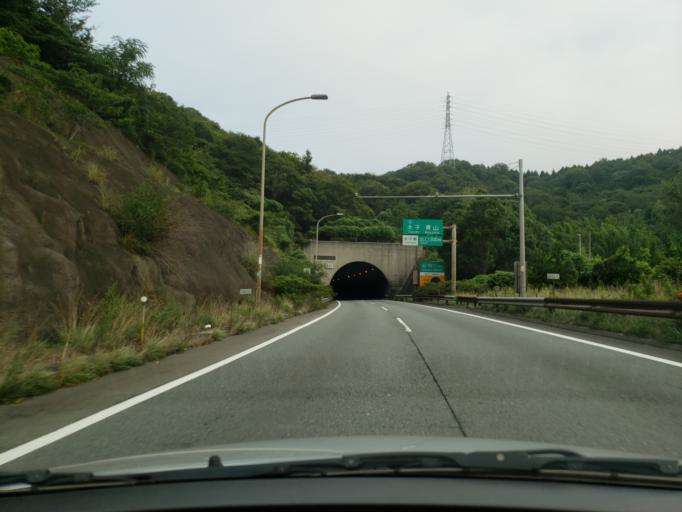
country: JP
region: Hyogo
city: Himeji
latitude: 34.8325
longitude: 134.6304
